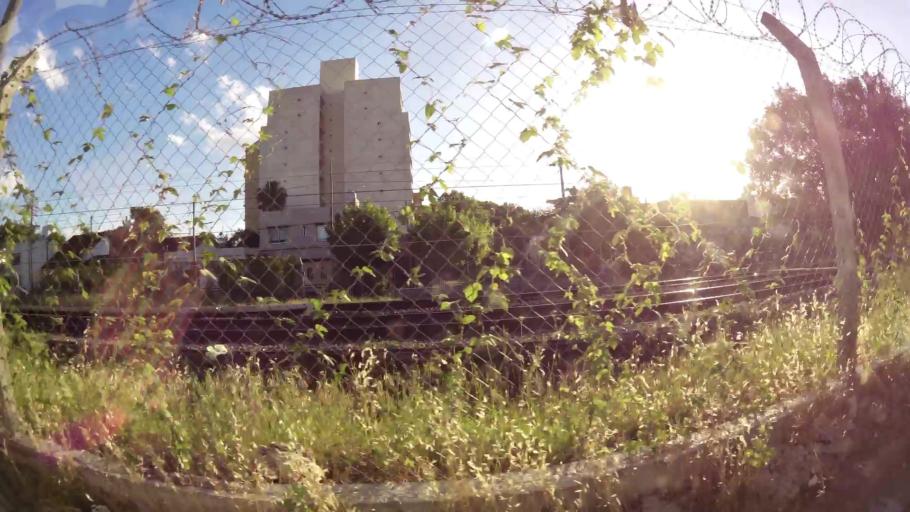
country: AR
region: Buenos Aires
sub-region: Partido de General San Martin
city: General San Martin
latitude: -34.5605
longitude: -58.5438
